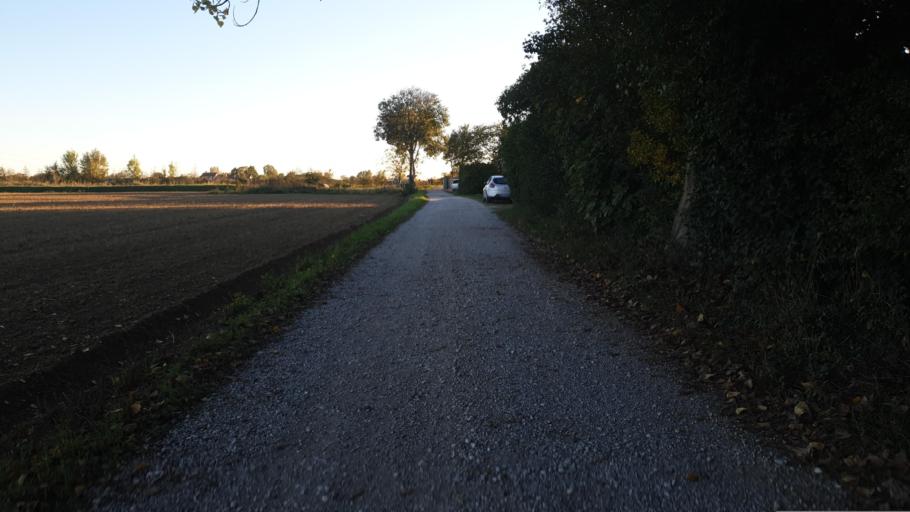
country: IT
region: Veneto
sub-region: Provincia di Venezia
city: Marano
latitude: 45.4466
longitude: 12.1002
